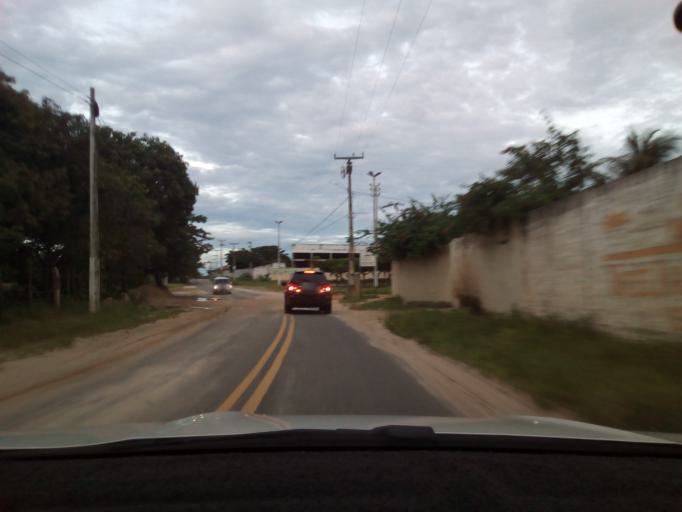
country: BR
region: Ceara
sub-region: Beberibe
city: Beberibe
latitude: -4.1861
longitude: -38.1194
